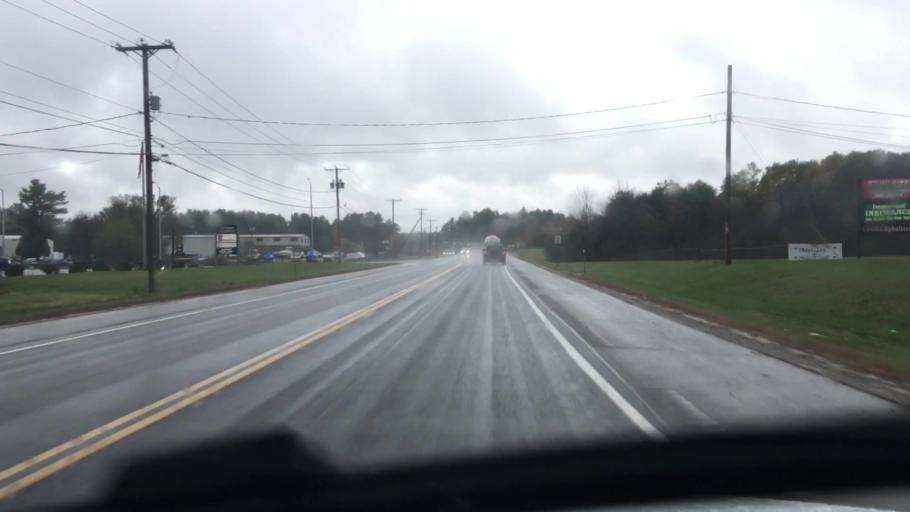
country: US
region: New Hampshire
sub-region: Strafford County
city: Rochester
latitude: 43.2433
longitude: -70.9865
